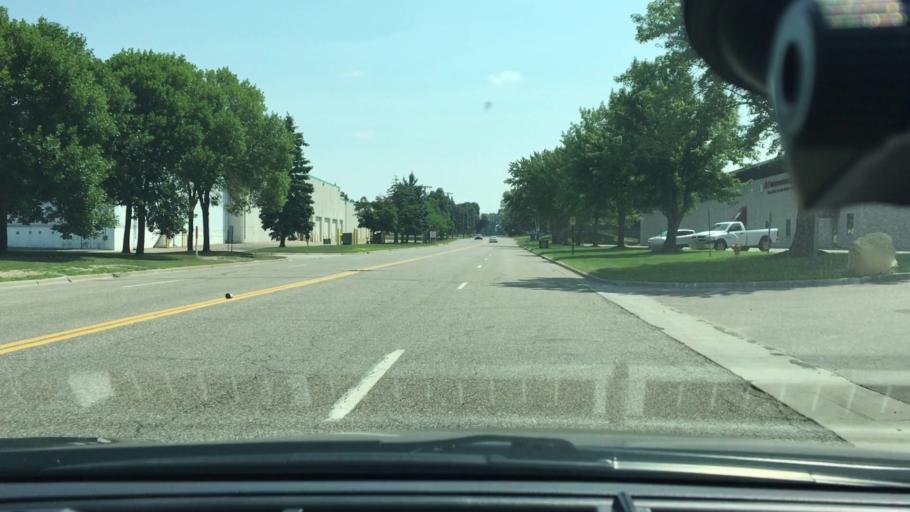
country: US
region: Minnesota
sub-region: Hennepin County
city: Plymouth
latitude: 44.9894
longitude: -93.4090
